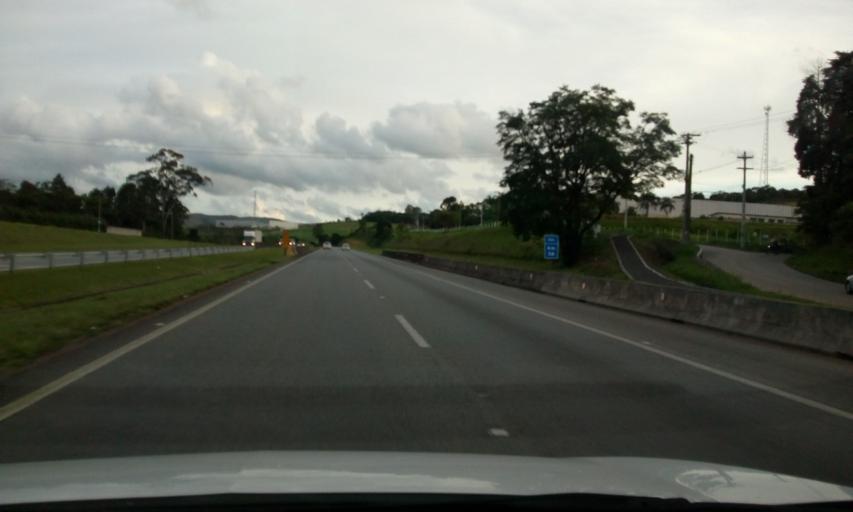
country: BR
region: Sao Paulo
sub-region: Bom Jesus Dos Perdoes
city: Bom Jesus dos Perdoes
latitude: -23.1636
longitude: -46.4466
